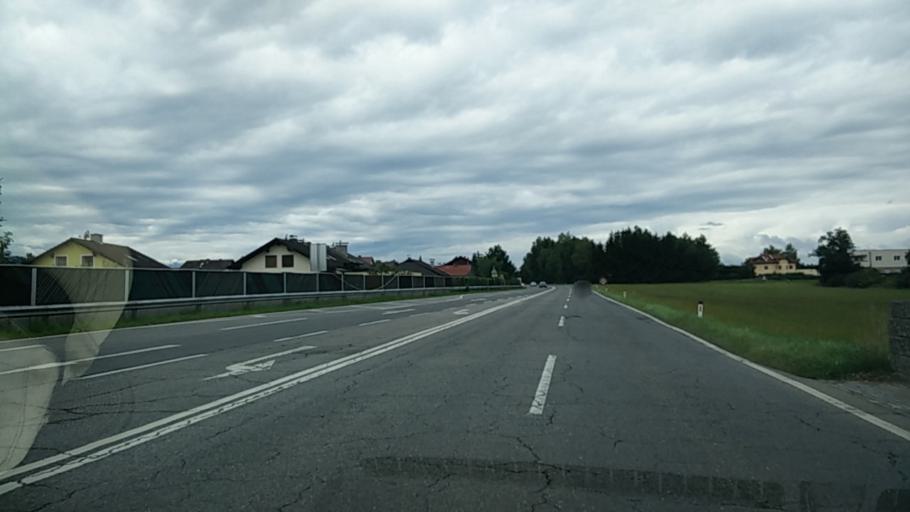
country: AT
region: Carinthia
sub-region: Politischer Bezirk Klagenfurt Land
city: Poggersdorf
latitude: 46.6287
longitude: 14.4074
